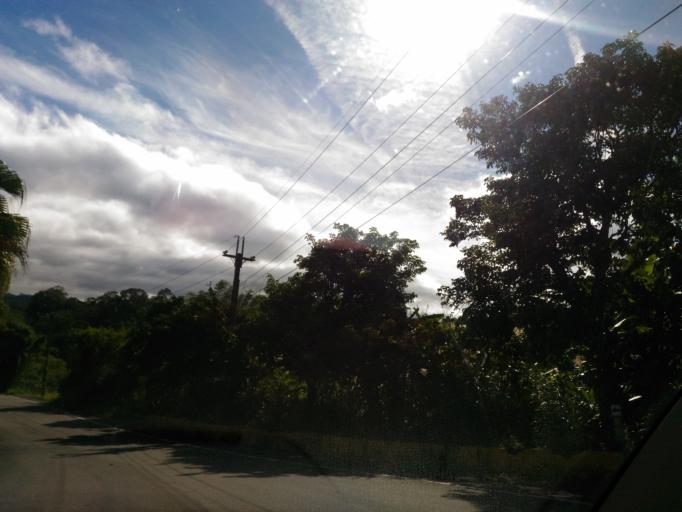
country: TW
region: Taiwan
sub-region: Hsinchu
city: Hsinchu
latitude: 24.7107
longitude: 121.0715
